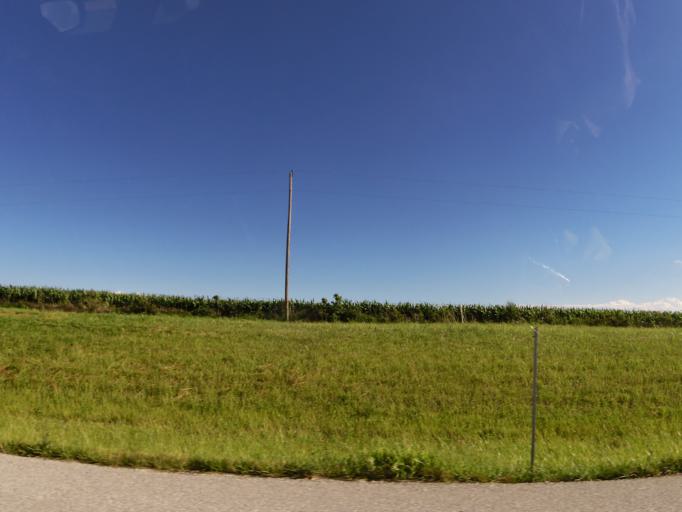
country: US
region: Missouri
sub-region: Marion County
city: Palmyra
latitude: 39.7435
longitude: -91.4864
